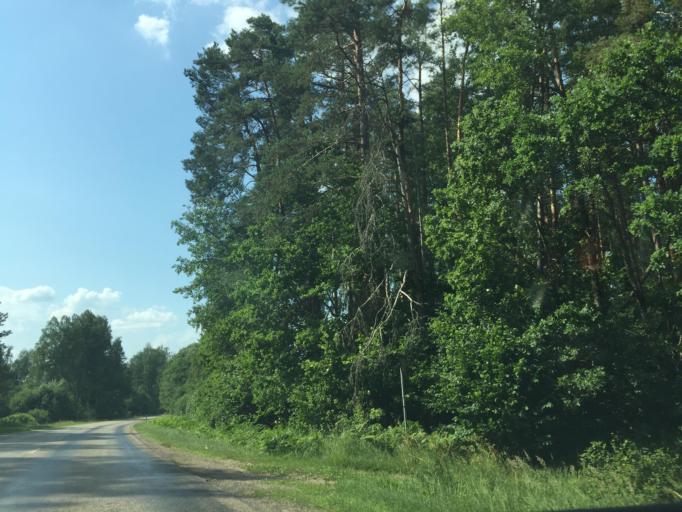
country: LV
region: Pargaujas
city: Stalbe
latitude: 57.3850
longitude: 24.9996
